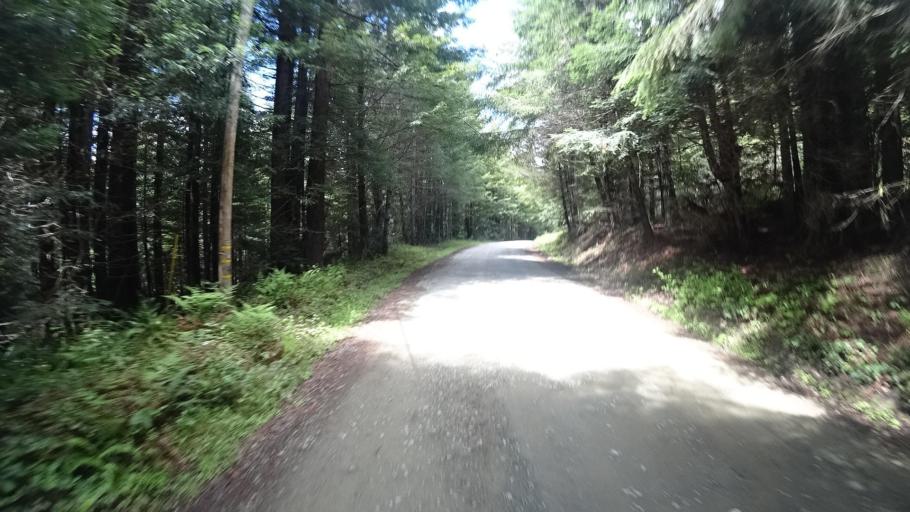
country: US
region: California
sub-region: Humboldt County
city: Blue Lake
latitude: 40.8057
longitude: -123.8833
